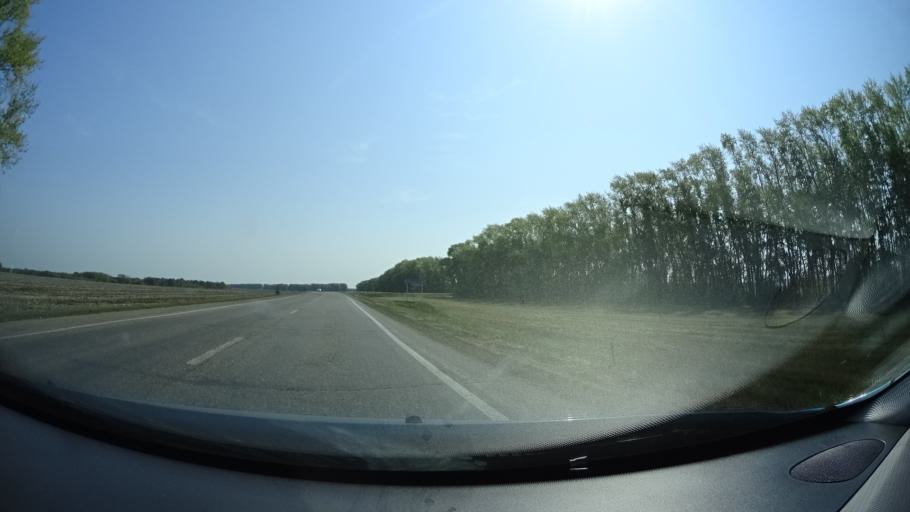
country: RU
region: Bashkortostan
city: Karmaskaly
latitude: 54.3900
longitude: 56.1249
